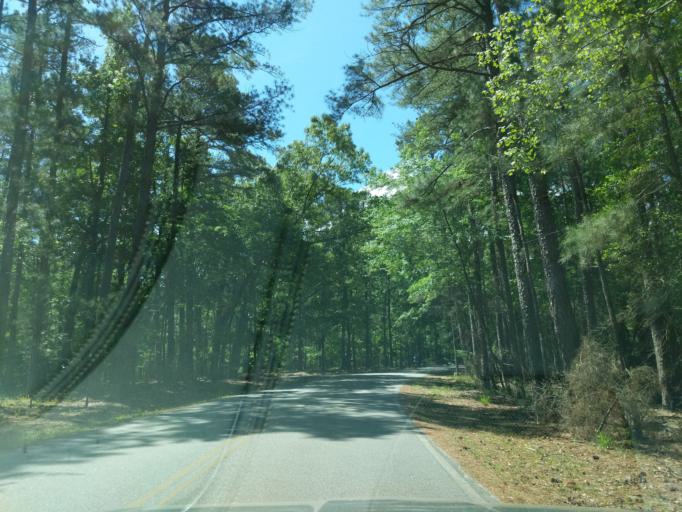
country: US
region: Georgia
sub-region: Columbia County
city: Appling
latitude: 33.6617
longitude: -82.3831
